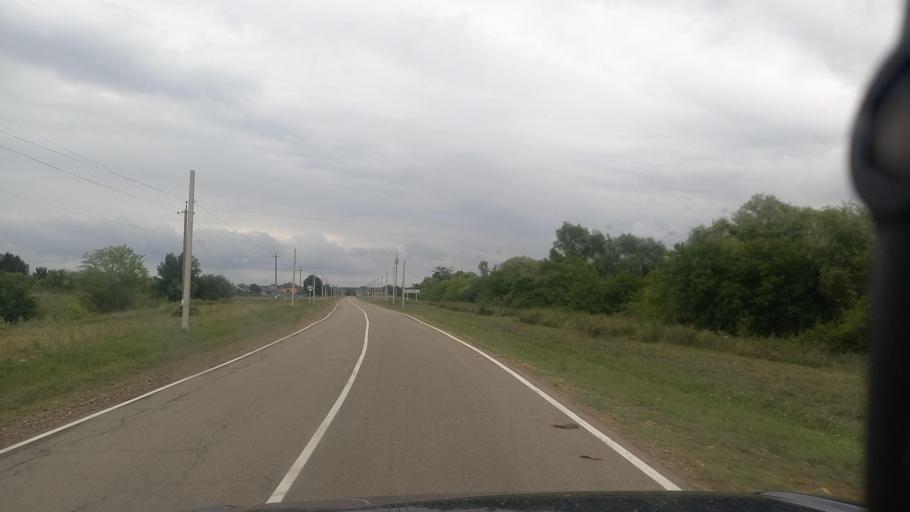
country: RU
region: Adygeya
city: Adygeysk
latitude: 44.8851
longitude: 39.2527
